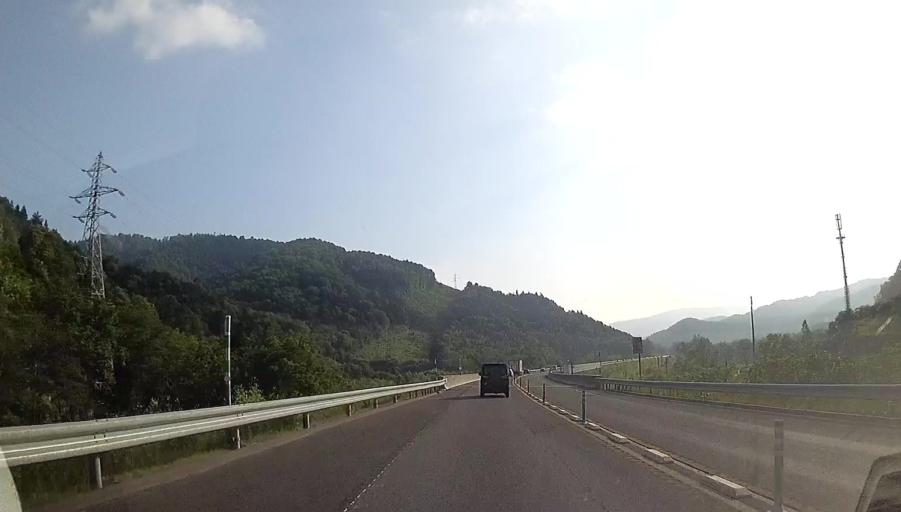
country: JP
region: Hokkaido
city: Shimo-furano
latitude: 43.0242
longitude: 142.4498
